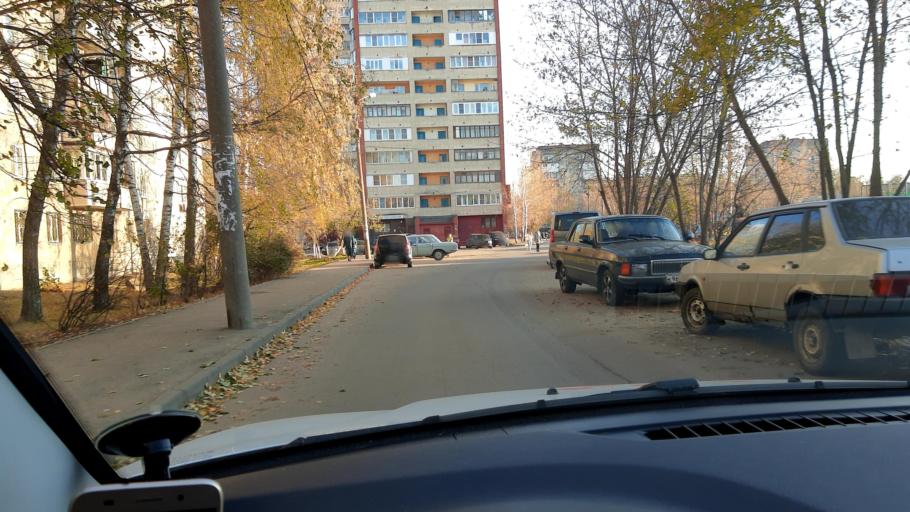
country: RU
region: Nizjnij Novgorod
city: Burevestnik
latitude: 56.2295
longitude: 43.8653
